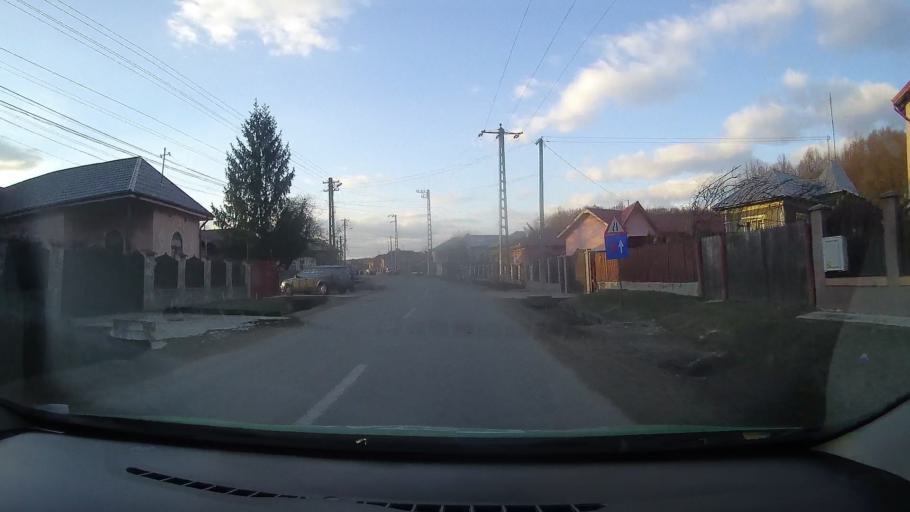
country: RO
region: Dambovita
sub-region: Comuna Gura Ocnitei
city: Adanca
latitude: 44.9244
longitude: 25.6074
